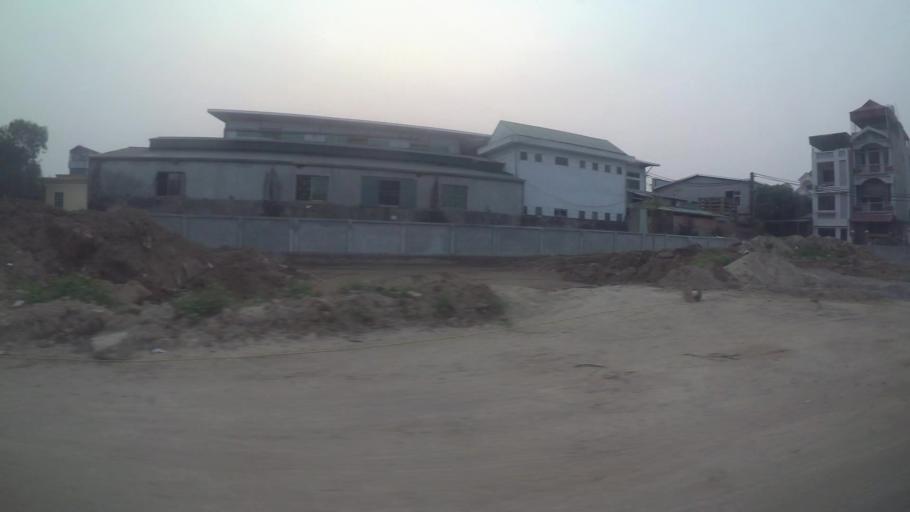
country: VN
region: Ha Noi
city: Ha Dong
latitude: 20.9949
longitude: 105.7307
